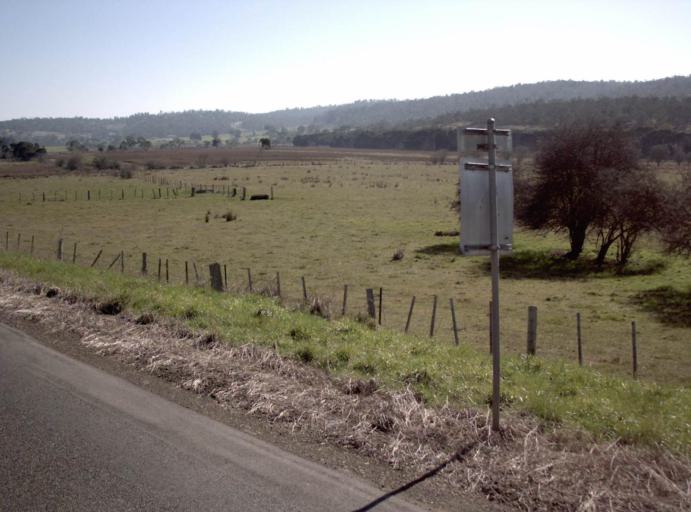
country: AU
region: Tasmania
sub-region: Launceston
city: Mayfield
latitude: -41.3290
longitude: 147.0700
